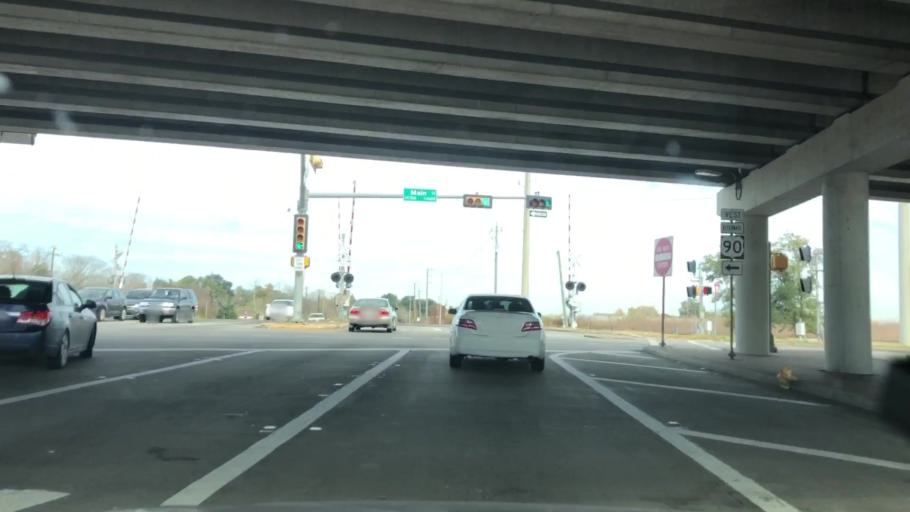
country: US
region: Texas
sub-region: Fort Bend County
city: Missouri City
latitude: 29.6305
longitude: -95.5074
